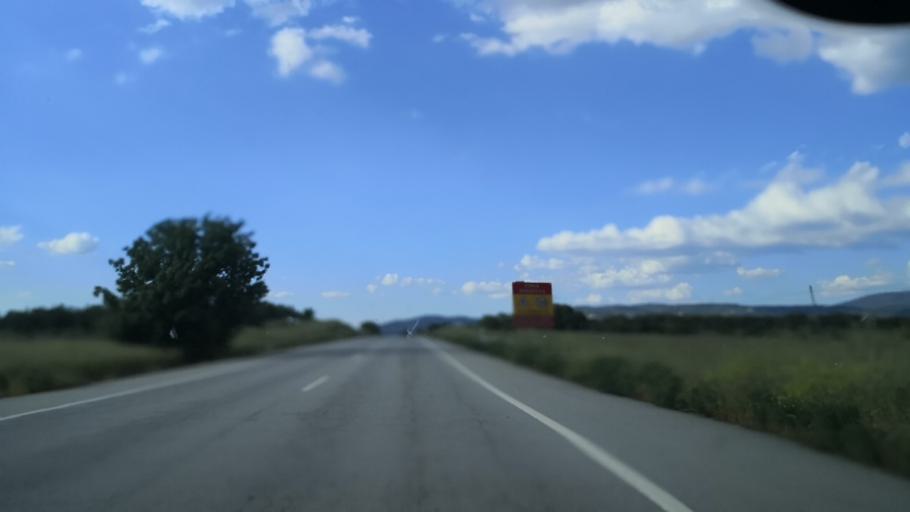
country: PT
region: Portalegre
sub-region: Portalegre
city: Portalegre
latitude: 39.2501
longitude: -7.4485
